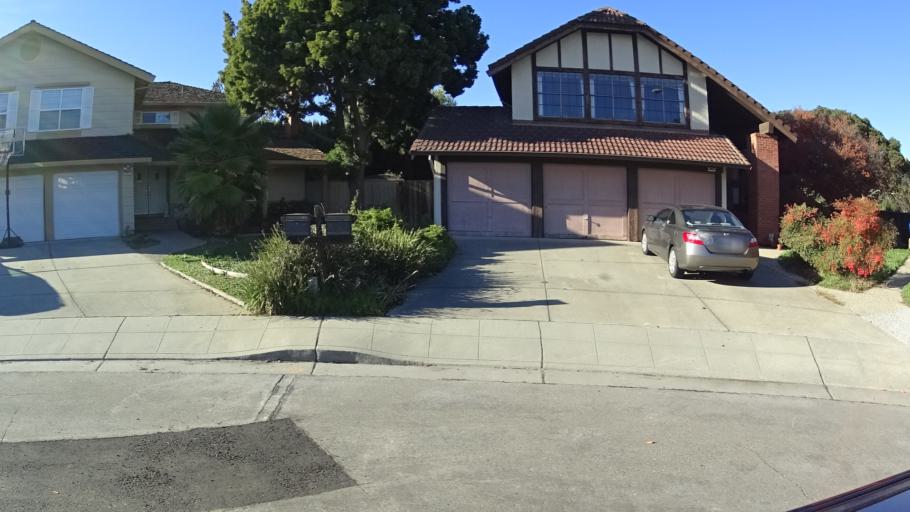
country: US
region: California
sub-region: Santa Clara County
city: Cupertino
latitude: 37.3397
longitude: -122.0251
